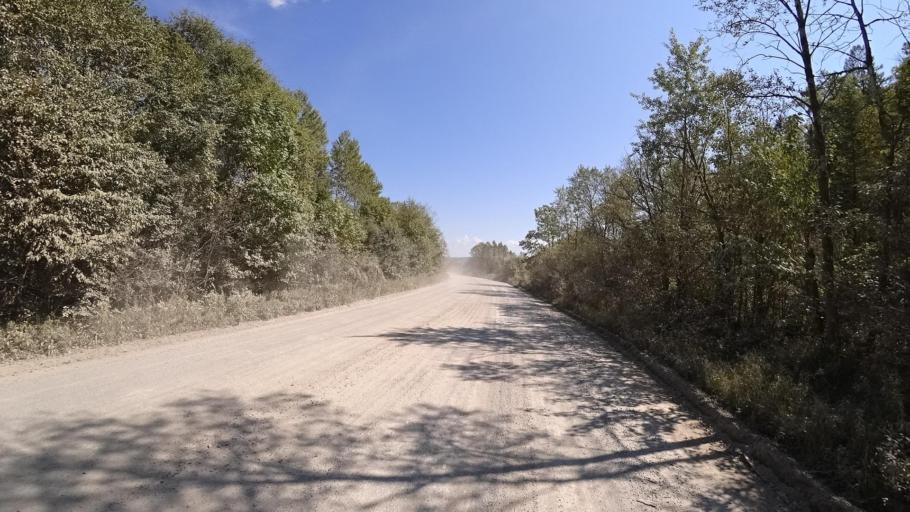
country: RU
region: Jewish Autonomous Oblast
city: Londoko
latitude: 49.0048
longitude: 131.9159
